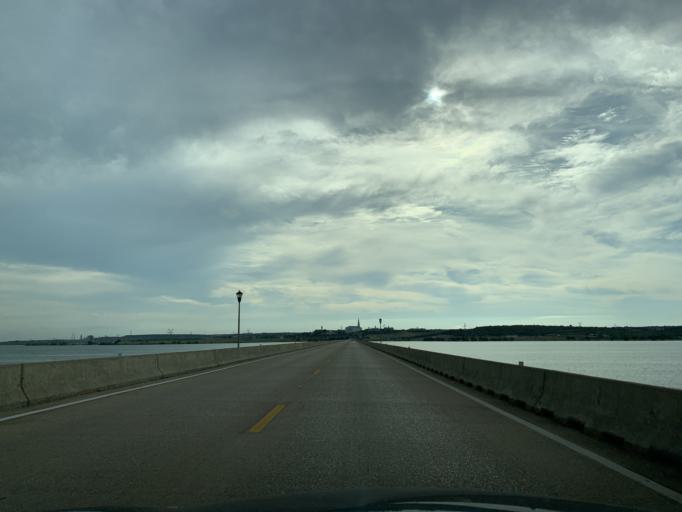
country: US
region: Texas
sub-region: Dallas County
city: Grand Prairie
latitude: 32.7066
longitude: -96.9699
